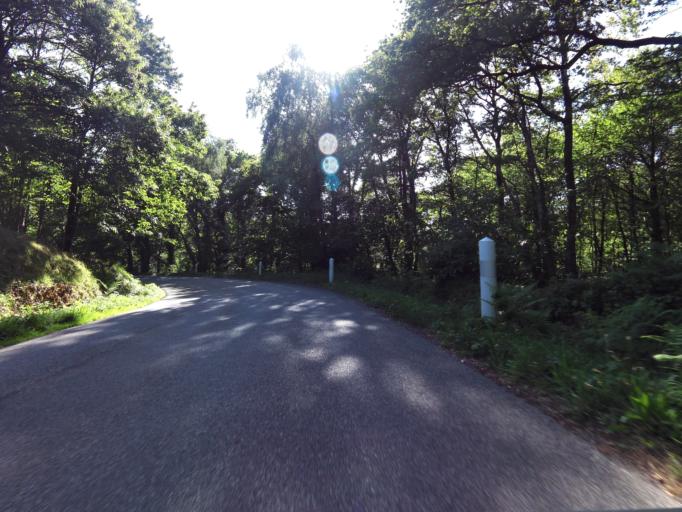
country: FR
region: Brittany
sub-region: Departement du Morbihan
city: Caden
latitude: 47.6297
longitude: -2.2958
